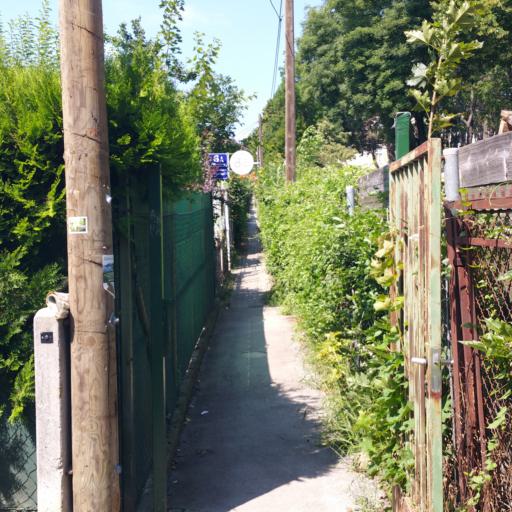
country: AT
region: Vienna
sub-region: Wien Stadt
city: Vienna
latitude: 48.2090
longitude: 16.2986
